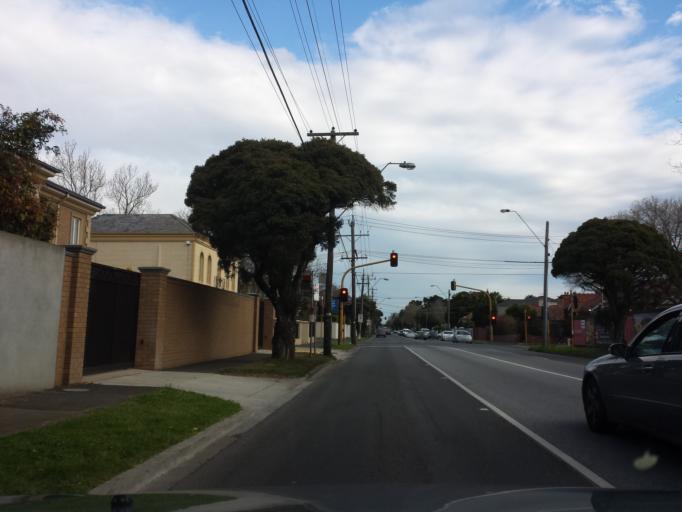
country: AU
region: Victoria
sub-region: Port Phillip
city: Elwood
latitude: -37.8952
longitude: 144.9901
